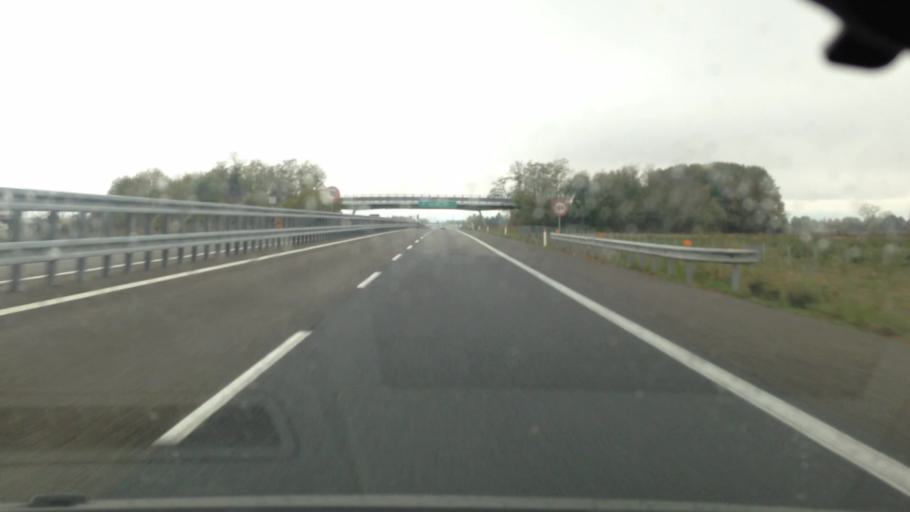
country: IT
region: Piedmont
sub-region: Provincia di Asti
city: Villanova d'Asti
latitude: 44.9512
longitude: 7.9406
